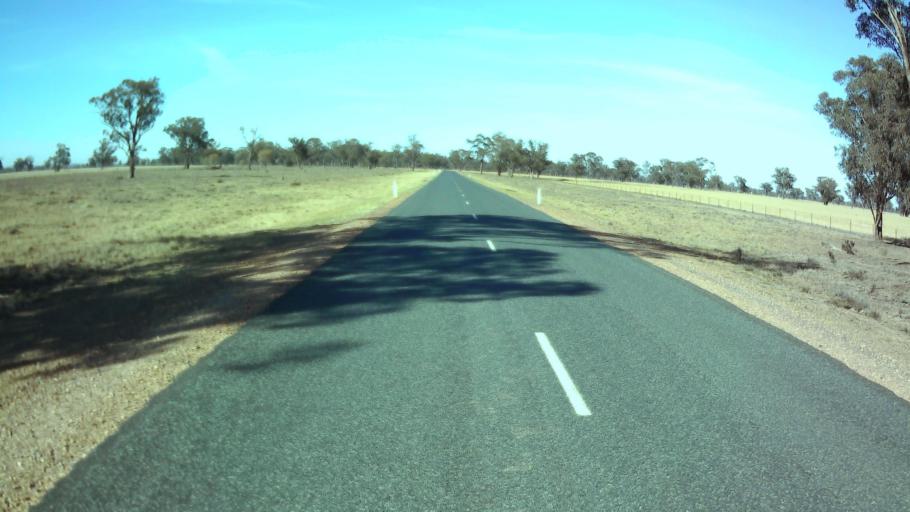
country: AU
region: New South Wales
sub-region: Weddin
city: Grenfell
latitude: -34.0551
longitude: 147.9150
